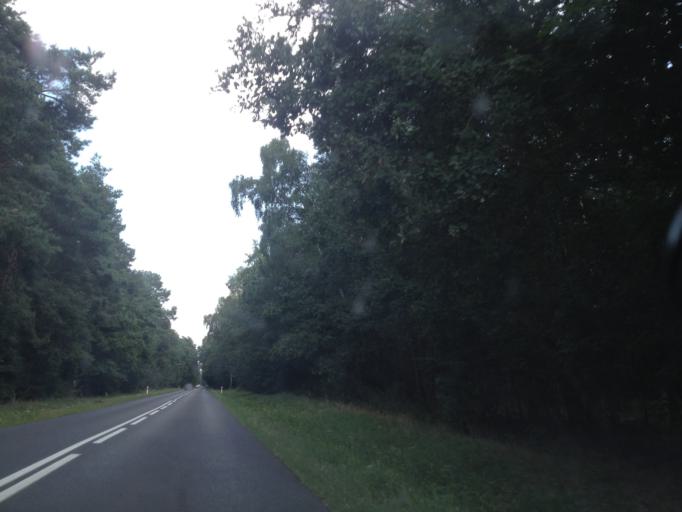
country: PL
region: Greater Poland Voivodeship
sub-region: Powiat poznanski
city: Kornik
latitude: 52.2422
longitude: 17.0191
